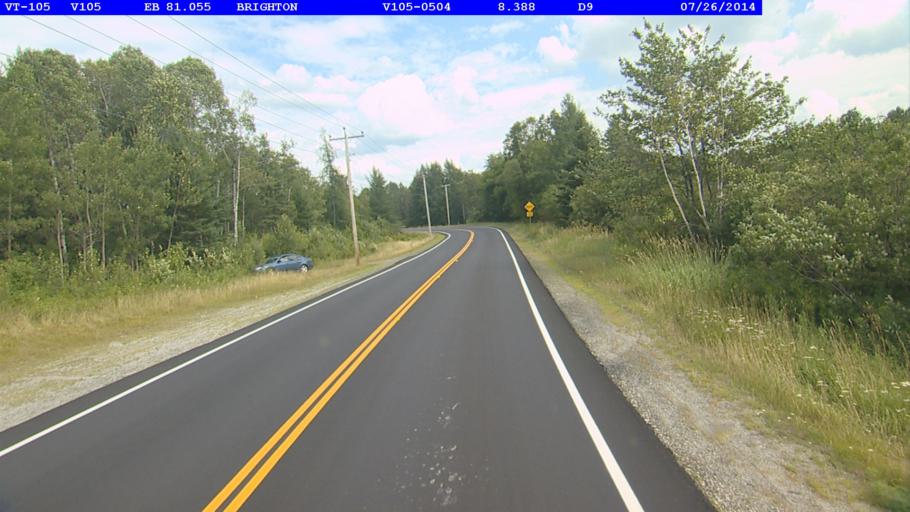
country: US
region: New Hampshire
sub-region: Coos County
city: Stratford
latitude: 44.7866
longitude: -71.8194
